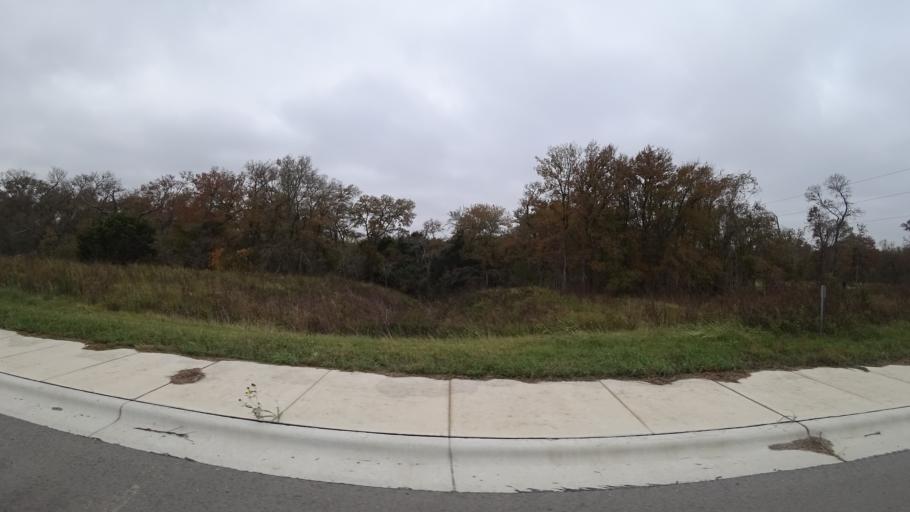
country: US
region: Texas
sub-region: Travis County
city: Pflugerville
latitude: 30.4079
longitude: -97.6121
